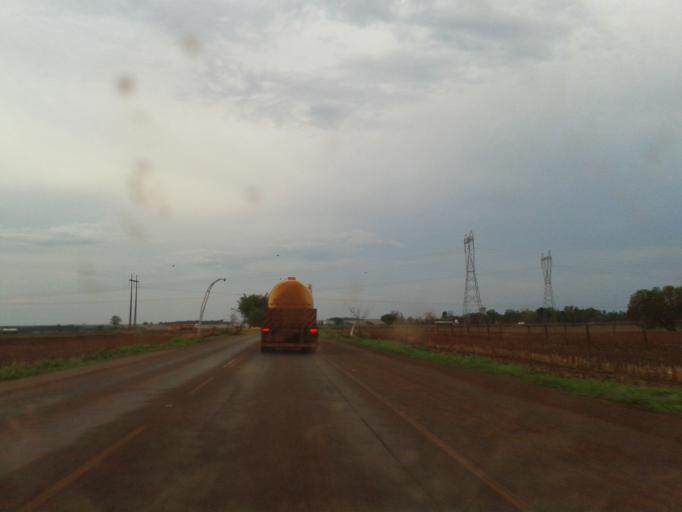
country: BR
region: Goias
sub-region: Santa Helena De Goias
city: Santa Helena de Goias
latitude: -17.9631
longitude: -50.4980
